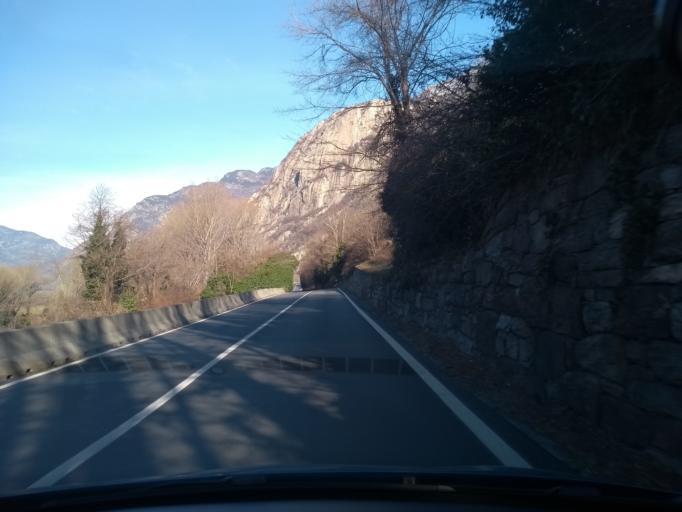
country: IT
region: Aosta Valley
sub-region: Valle d'Aosta
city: Hone
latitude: 45.6231
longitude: 7.7376
